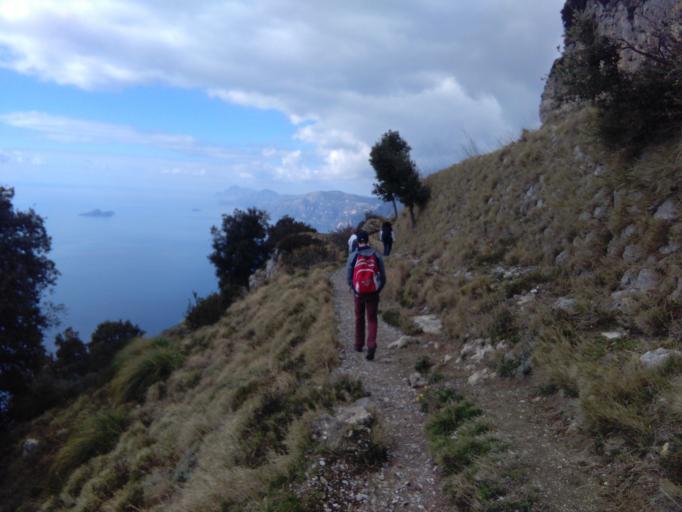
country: IT
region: Campania
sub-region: Provincia di Salerno
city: Praiano
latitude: 40.6217
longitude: 14.5205
